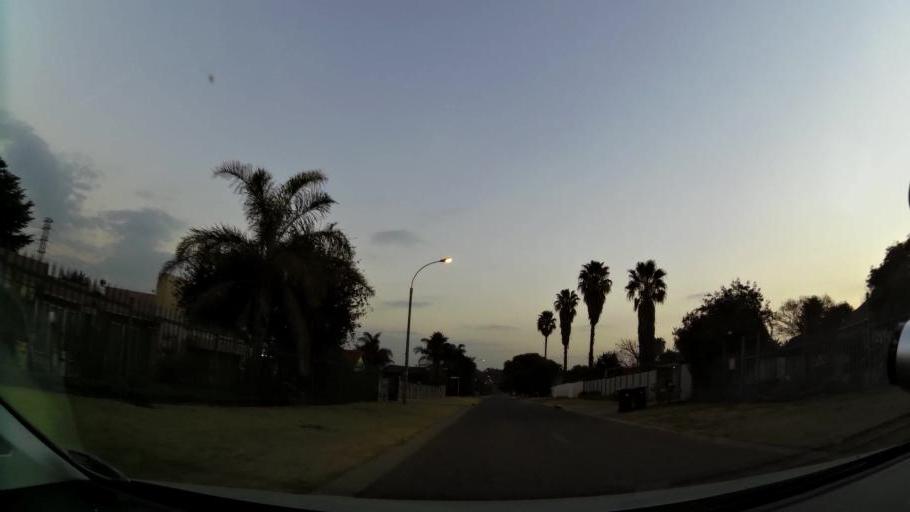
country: ZA
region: Gauteng
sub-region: Ekurhuleni Metropolitan Municipality
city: Tembisa
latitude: -26.0537
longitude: 28.2452
